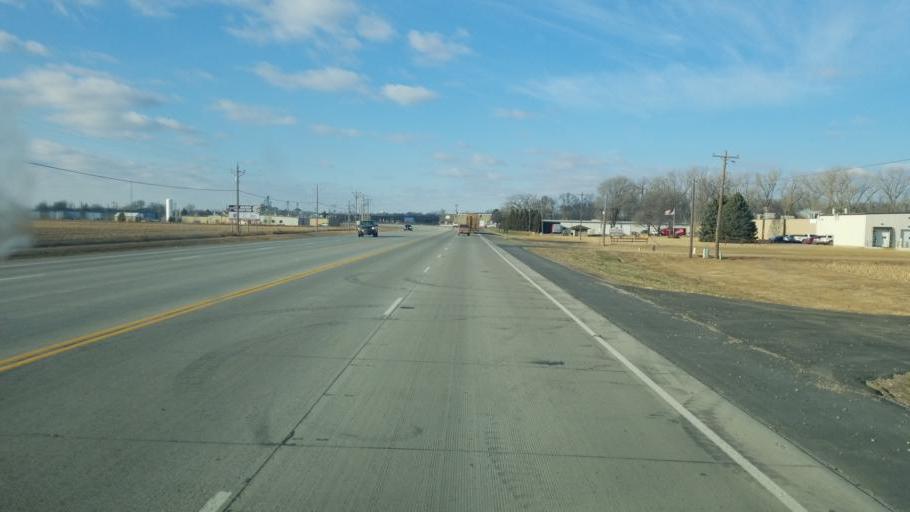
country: US
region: South Dakota
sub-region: Yankton County
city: Yankton
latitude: 42.8799
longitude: -97.3581
